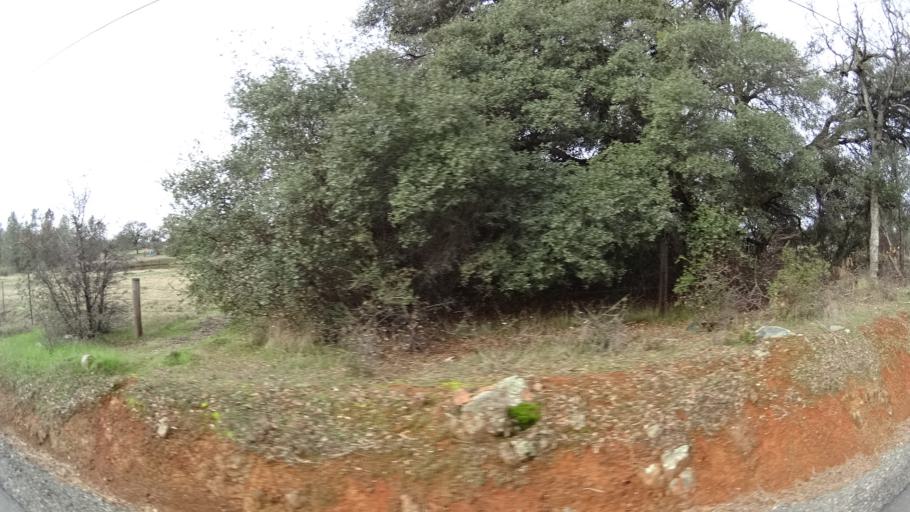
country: US
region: California
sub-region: Butte County
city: Oroville East
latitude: 39.4386
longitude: -121.4312
